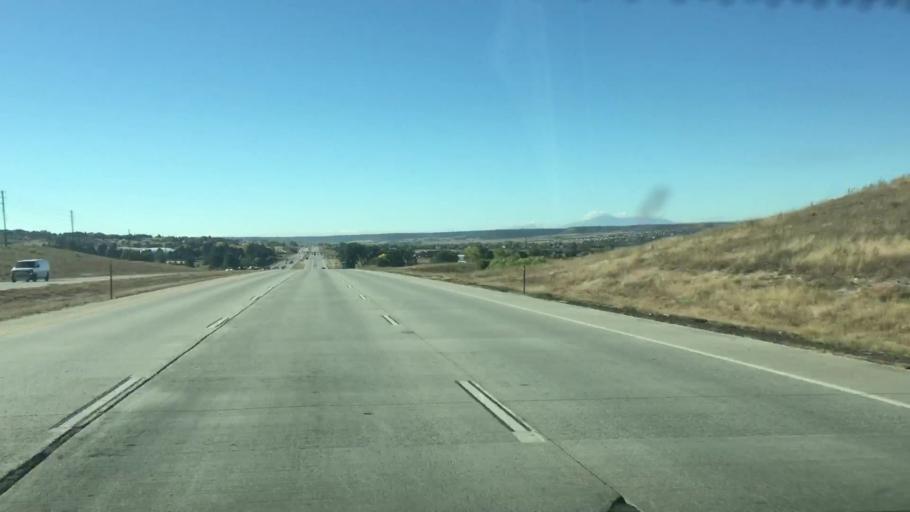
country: US
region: Colorado
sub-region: Douglas County
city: The Pinery
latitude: 39.4651
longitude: -104.7589
